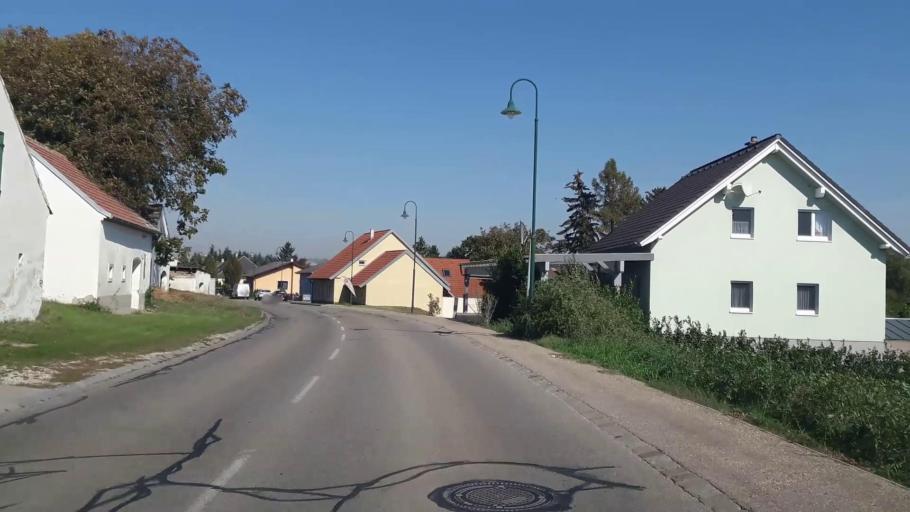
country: AT
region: Lower Austria
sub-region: Politischer Bezirk Korneuburg
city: Harmannsdorf
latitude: 48.3905
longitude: 16.3671
